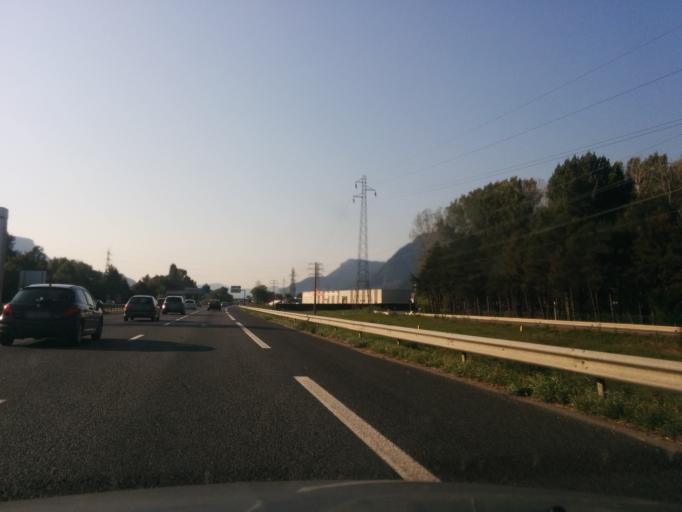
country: FR
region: Rhone-Alpes
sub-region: Departement de l'Isere
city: Saint-Egreve
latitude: 45.2303
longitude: 5.6660
